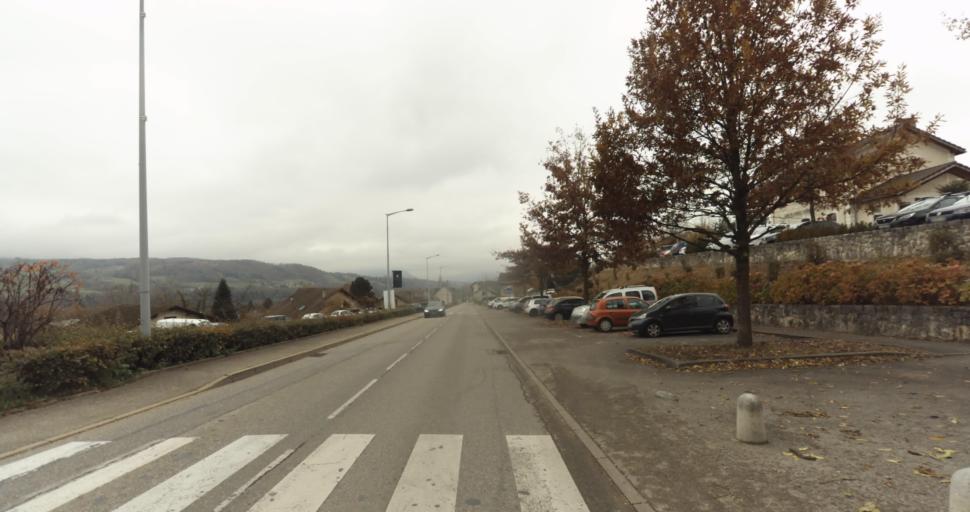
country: FR
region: Rhone-Alpes
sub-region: Departement de la Haute-Savoie
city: Groisy
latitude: 46.0114
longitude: 6.1762
